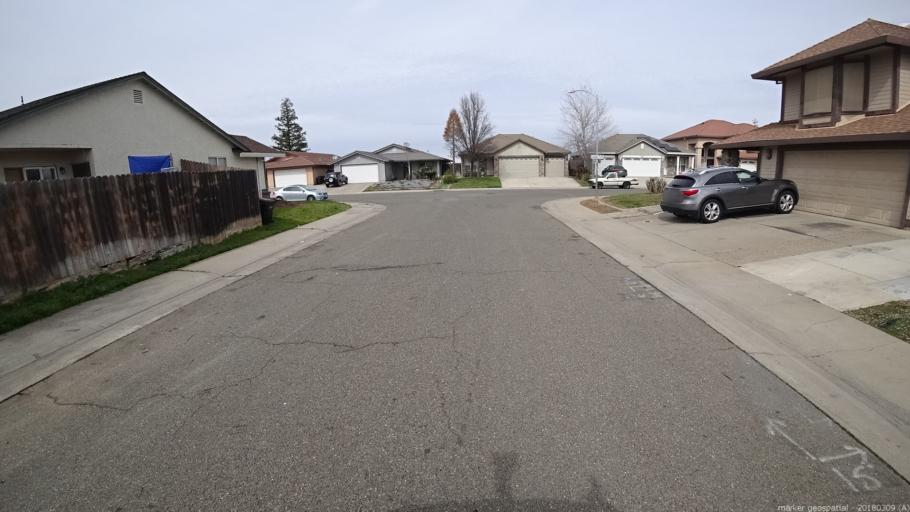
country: US
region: California
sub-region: Sacramento County
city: Vineyard
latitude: 38.4665
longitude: -121.3820
